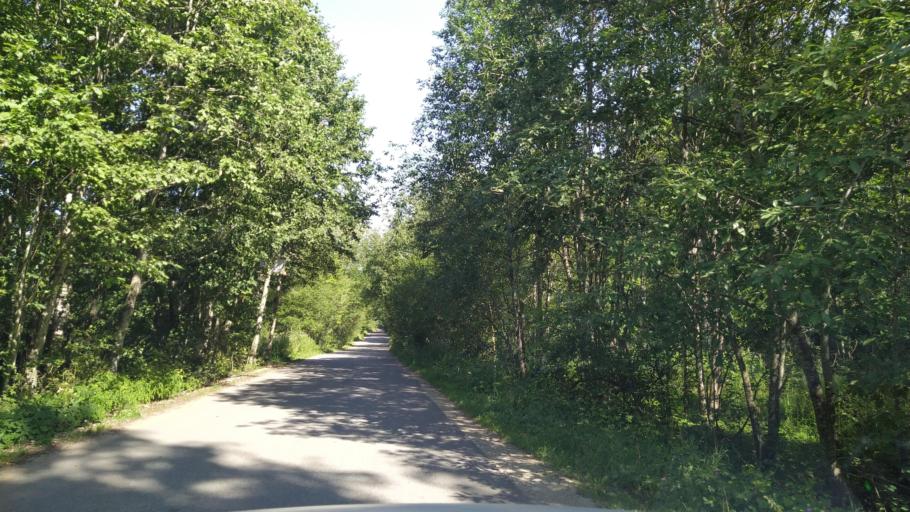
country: RU
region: Leningrad
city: Rozhdestveno
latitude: 59.2756
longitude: 30.0269
